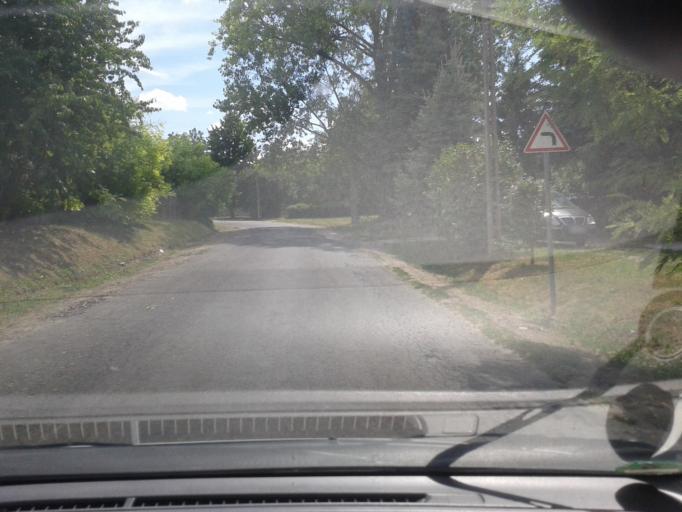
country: HU
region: Komarom-Esztergom
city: Pilismarot
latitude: 47.7880
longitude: 18.8753
